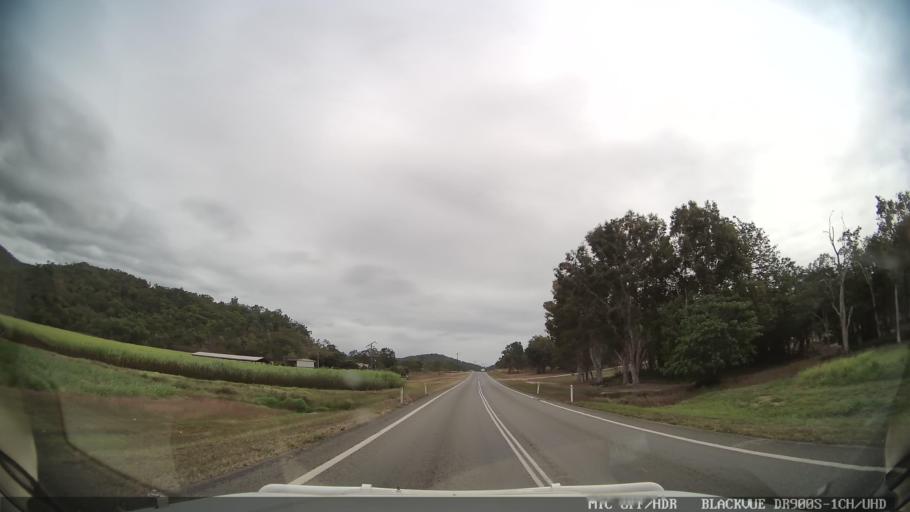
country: AU
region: Queensland
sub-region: Hinchinbrook
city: Ingham
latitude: -18.8607
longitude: 146.1677
